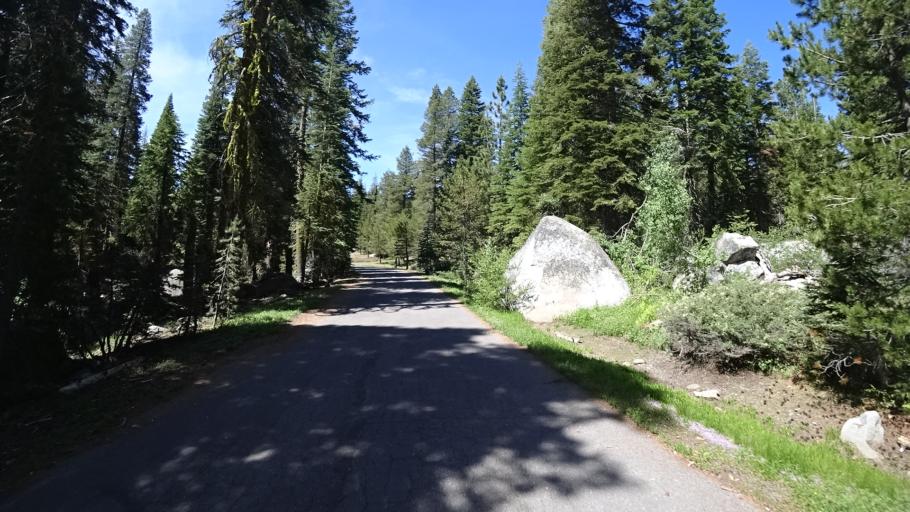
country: US
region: California
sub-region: Calaveras County
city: Arnold
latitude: 38.4415
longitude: -120.0796
